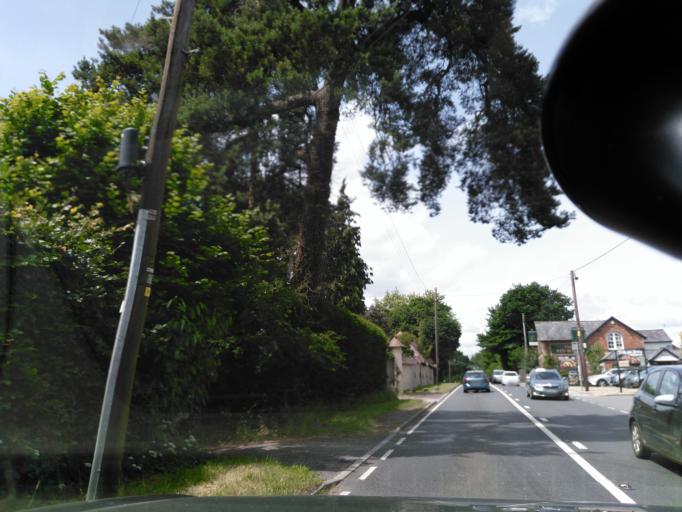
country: GB
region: England
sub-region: Hampshire
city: West Wellow
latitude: 50.9706
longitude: -1.5910
